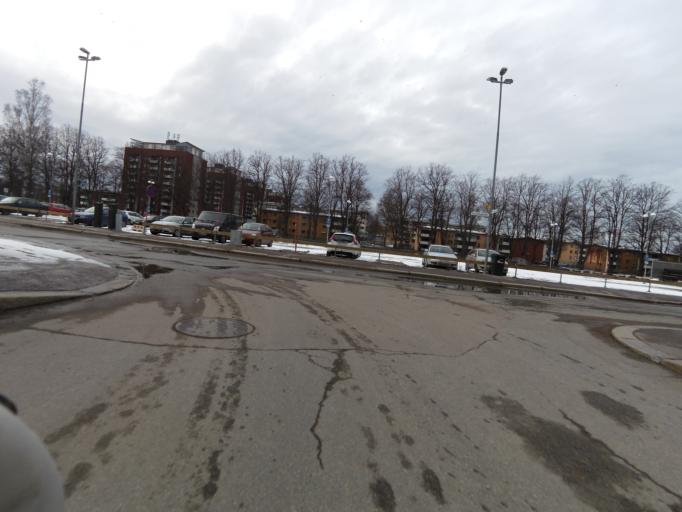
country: SE
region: Gaevleborg
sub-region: Gavle Kommun
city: Gavle
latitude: 60.6774
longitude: 17.1547
